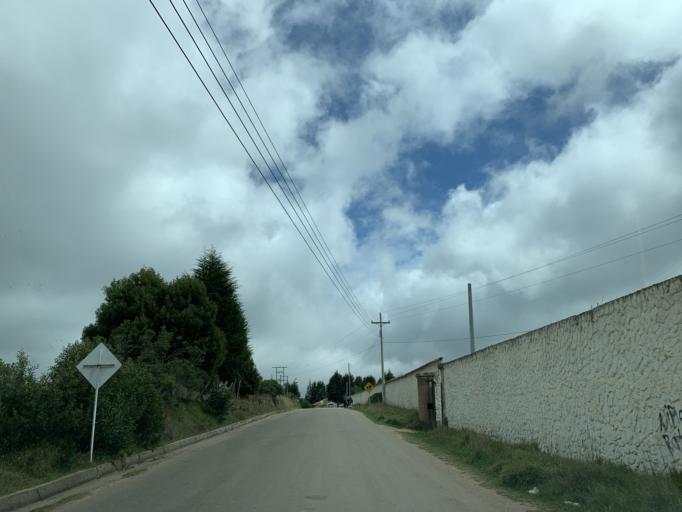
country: CO
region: Boyaca
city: Tunja
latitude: 5.5737
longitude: -73.3660
